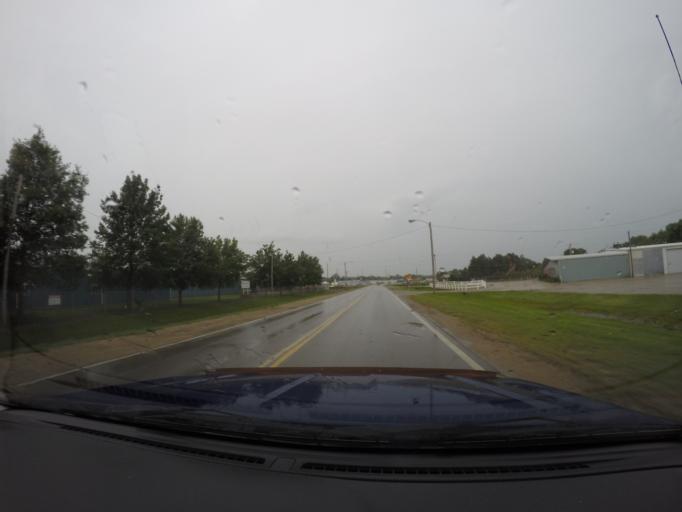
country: US
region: Kansas
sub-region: Cloud County
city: Concordia
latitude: 39.5728
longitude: -97.6345
